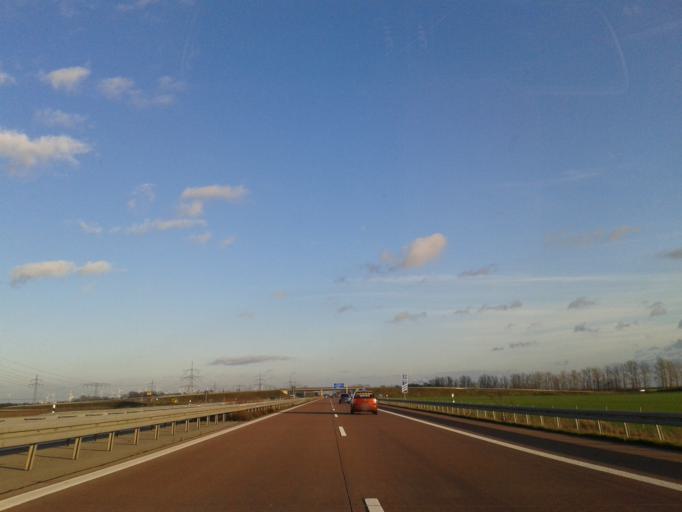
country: DE
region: Saxony-Anhalt
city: Schafstadt
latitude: 51.4004
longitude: 11.7623
